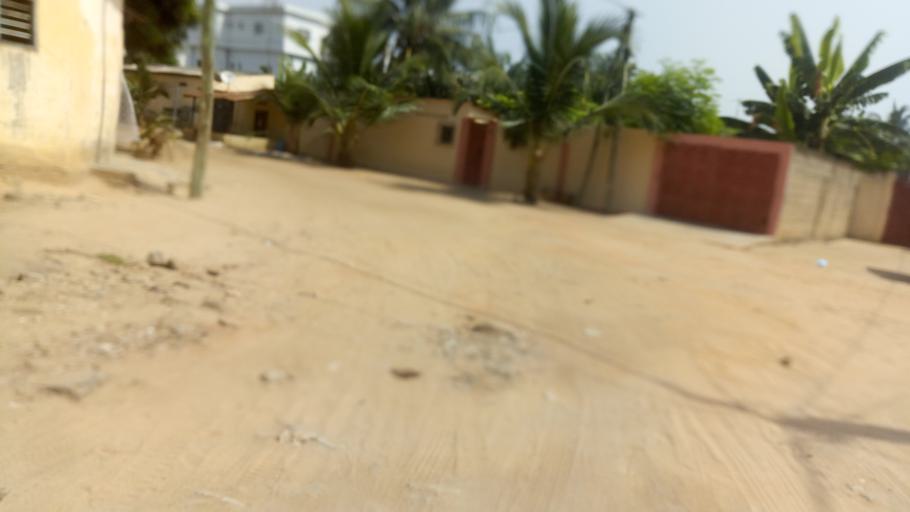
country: TG
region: Maritime
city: Lome
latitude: 6.1785
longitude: 1.1730
